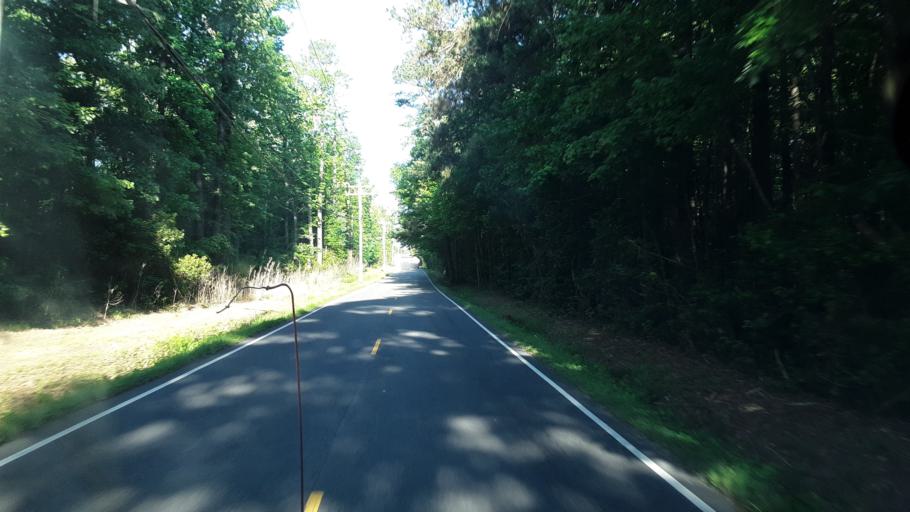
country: US
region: Virginia
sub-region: City of Virginia Beach
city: Virginia Beach
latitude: 36.7205
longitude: -76.0392
